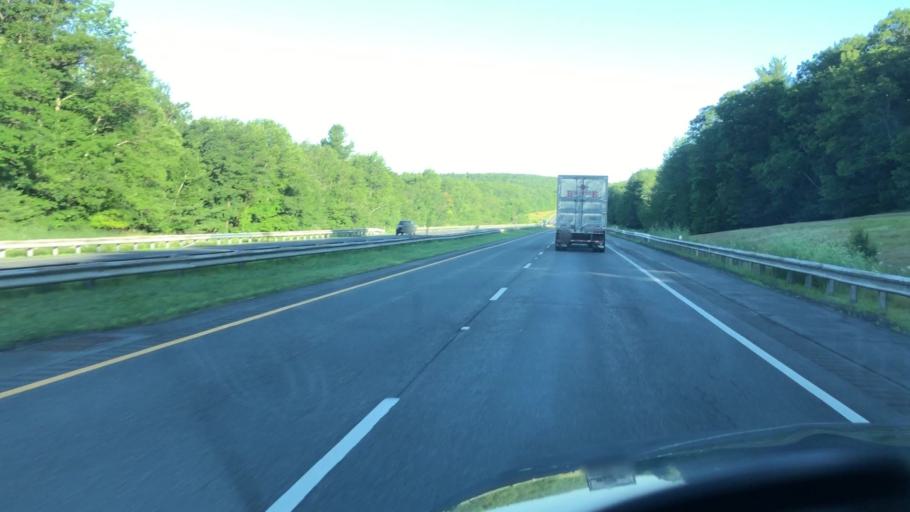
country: US
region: Massachusetts
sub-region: Berkshire County
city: Otis
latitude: 42.2281
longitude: -72.9748
